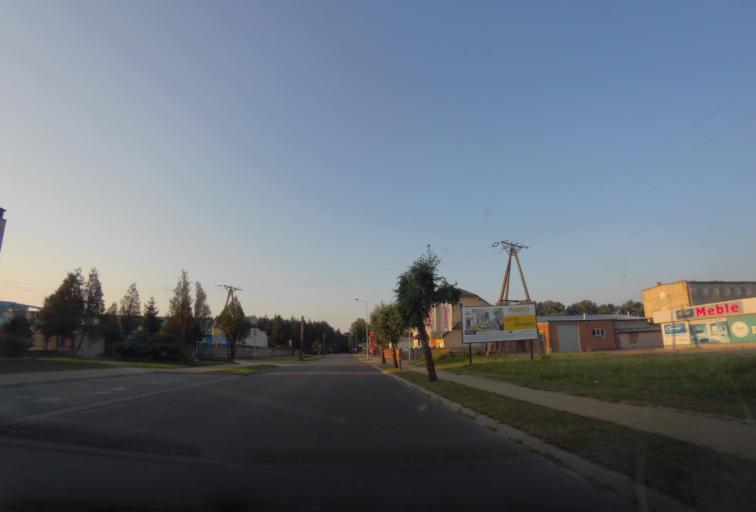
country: PL
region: Lublin Voivodeship
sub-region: Powiat janowski
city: Janow Lubelski
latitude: 50.6976
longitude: 22.4204
